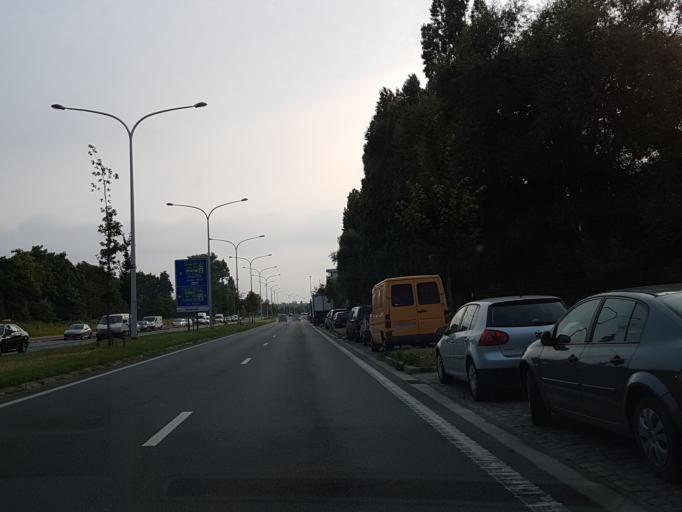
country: BE
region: Flanders
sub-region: Provincie Antwerpen
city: Antwerpen
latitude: 51.1946
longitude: 4.4268
